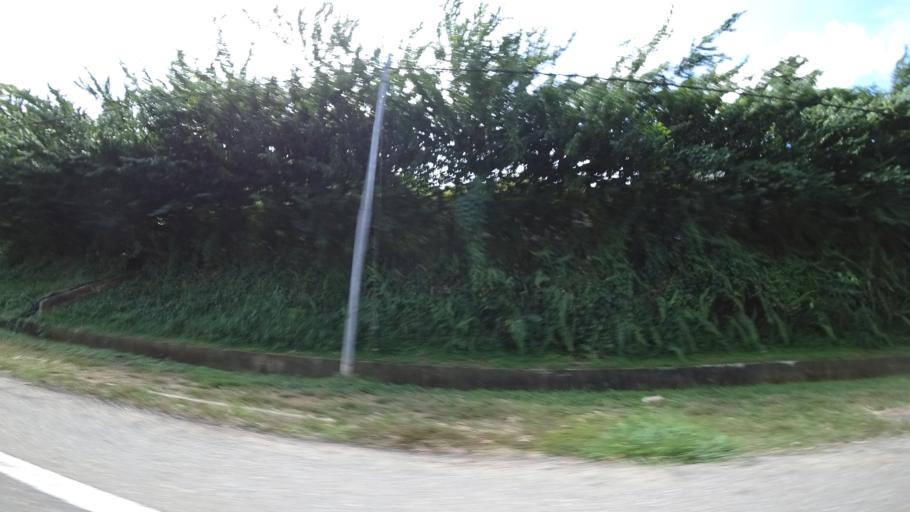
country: BN
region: Brunei and Muara
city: Bandar Seri Begawan
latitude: 4.8868
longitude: 114.9705
